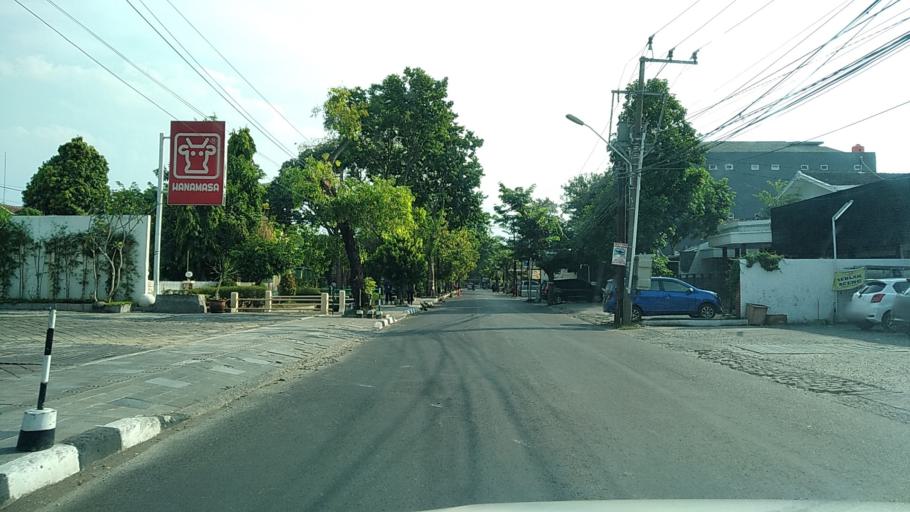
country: ID
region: Central Java
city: Semarang
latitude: -6.9938
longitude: 110.4285
